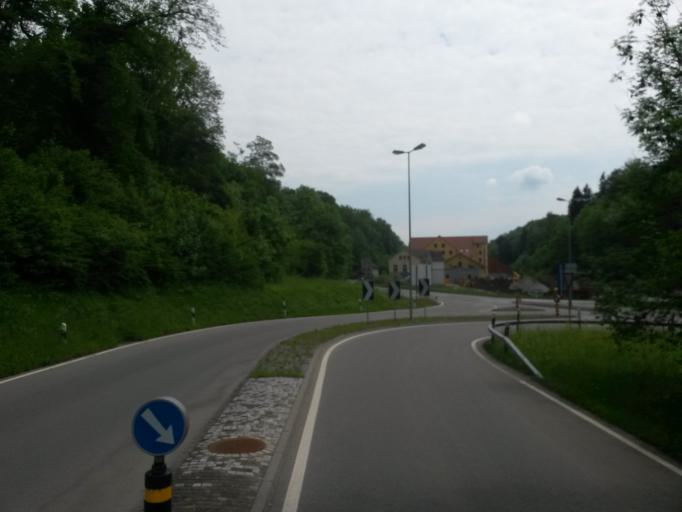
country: CH
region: Zurich
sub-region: Bezirk Pfaeffikon
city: Effretikon / Watt
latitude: 47.4327
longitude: 8.7043
